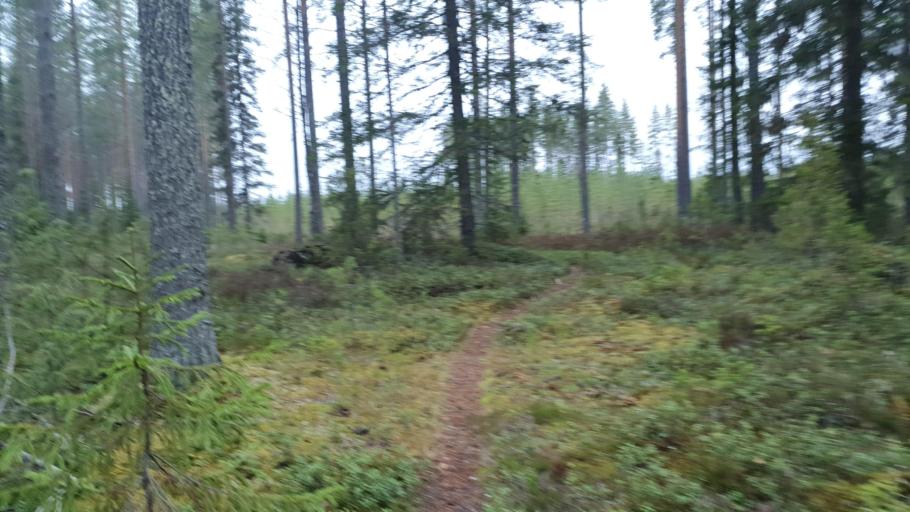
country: FI
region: Kainuu
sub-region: Kehys-Kainuu
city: Kuhmo
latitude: 64.1323
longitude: 29.3903
